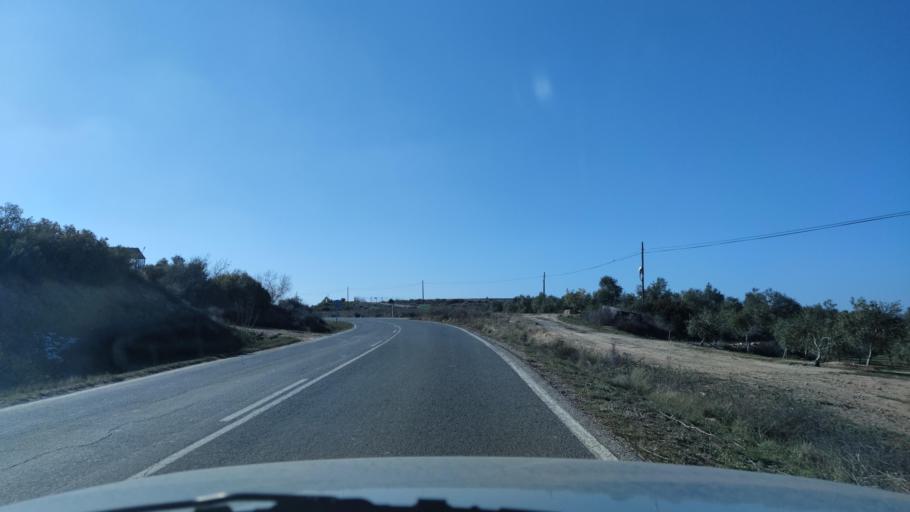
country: ES
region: Catalonia
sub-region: Provincia de Lleida
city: Maials
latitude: 41.3574
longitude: 0.4746
